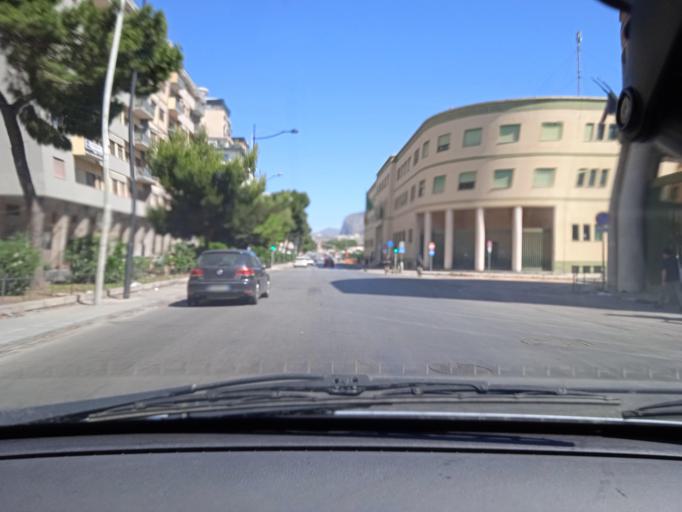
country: IT
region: Sicily
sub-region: Palermo
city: Palermo
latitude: 38.1250
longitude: 13.3638
